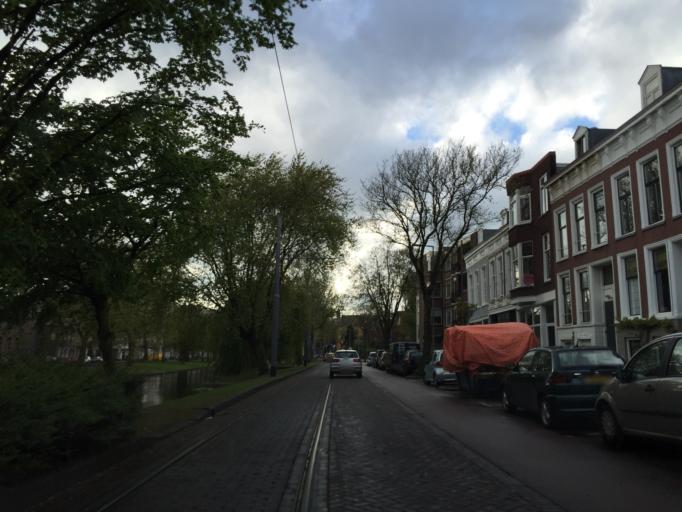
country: NL
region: South Holland
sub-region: Gemeente Rotterdam
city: Rotterdam
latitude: 51.9300
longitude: 4.4802
